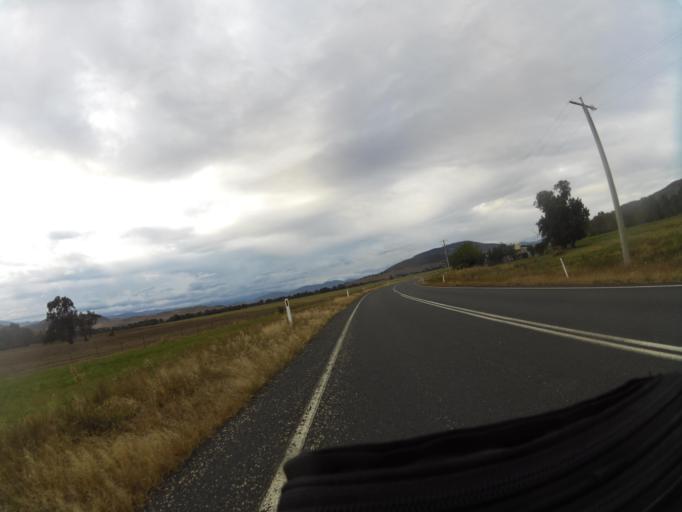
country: AU
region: New South Wales
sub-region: Snowy River
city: Jindabyne
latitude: -36.0930
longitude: 147.9819
